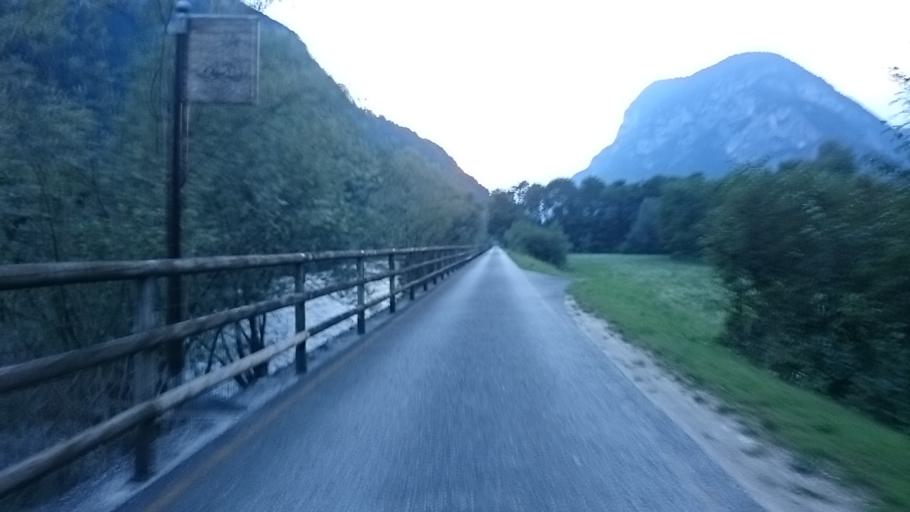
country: IT
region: Trentino-Alto Adige
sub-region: Provincia di Trento
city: Grigno
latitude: 45.9999
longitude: 11.6548
